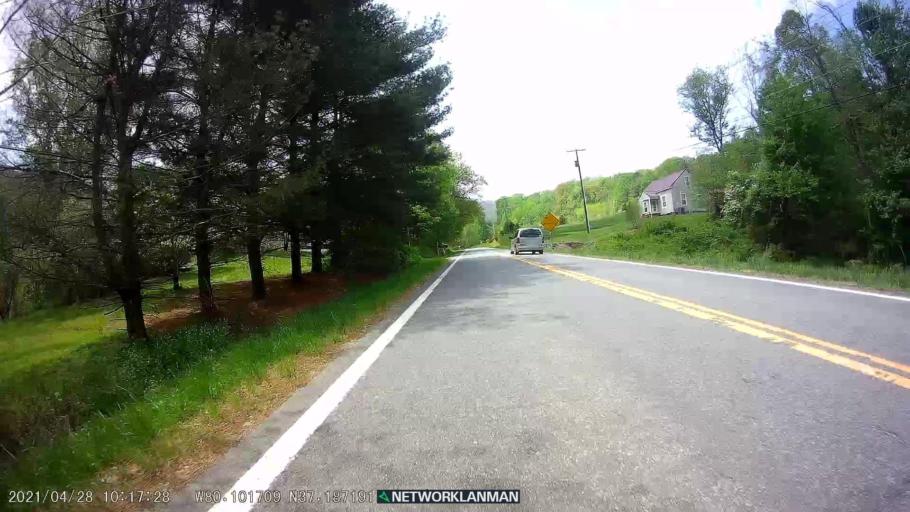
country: US
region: Virginia
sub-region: Roanoke County
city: Cave Spring
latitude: 37.1872
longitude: -80.1013
